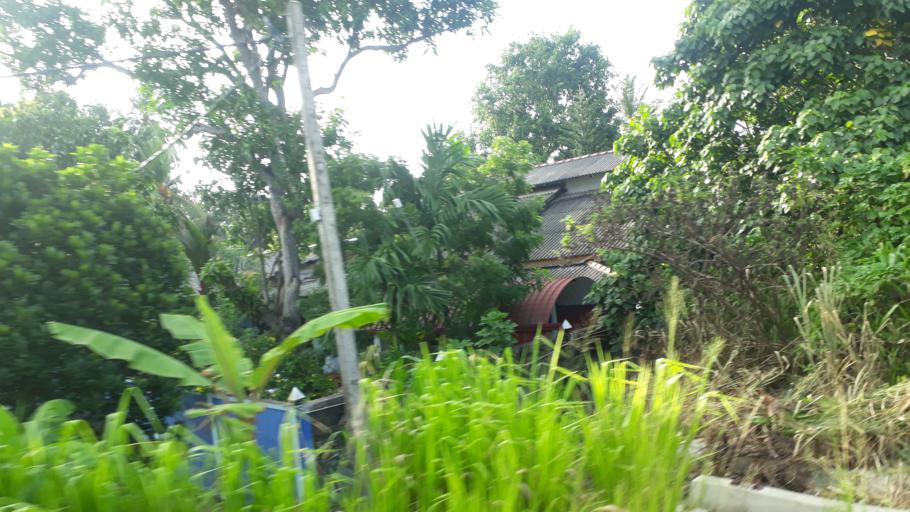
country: LK
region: Western
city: Kolonnawa
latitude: 6.9477
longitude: 79.8869
